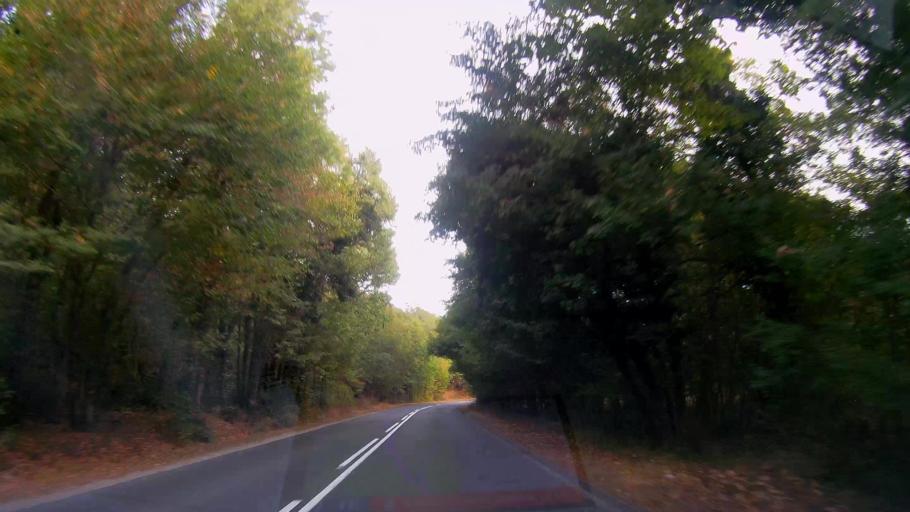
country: BG
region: Burgas
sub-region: Obshtina Primorsko
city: Primorsko
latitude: 42.3093
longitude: 27.7241
